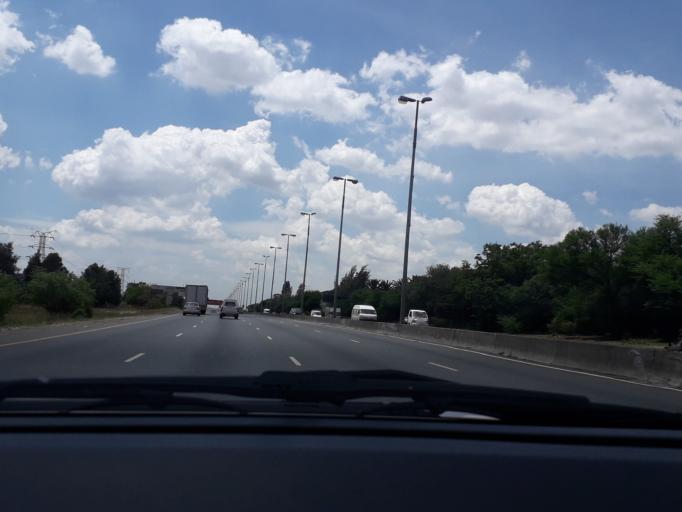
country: ZA
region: Gauteng
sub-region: City of Johannesburg Metropolitan Municipality
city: Johannesburg
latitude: -26.2499
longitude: 27.9989
